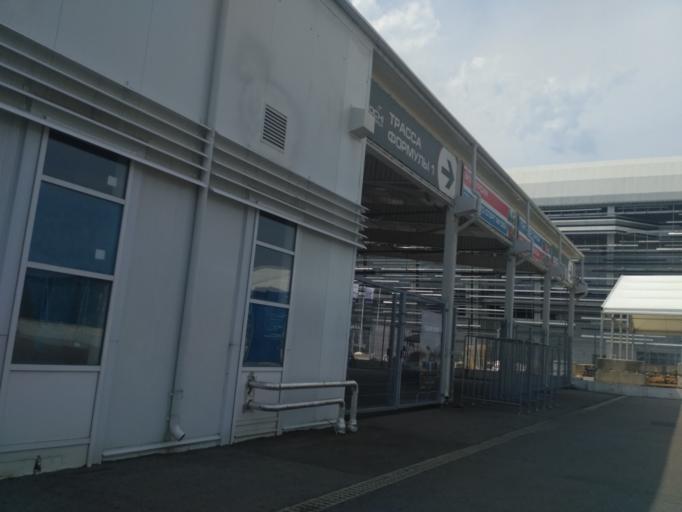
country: RU
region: Krasnodarskiy
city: Adler
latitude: 43.4106
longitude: 39.9711
